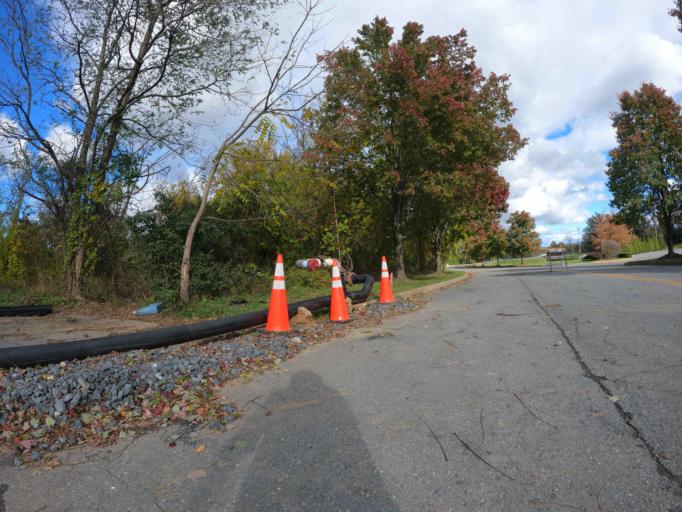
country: US
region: Maryland
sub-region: Carroll County
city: Mount Airy
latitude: 39.3743
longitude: -77.1467
